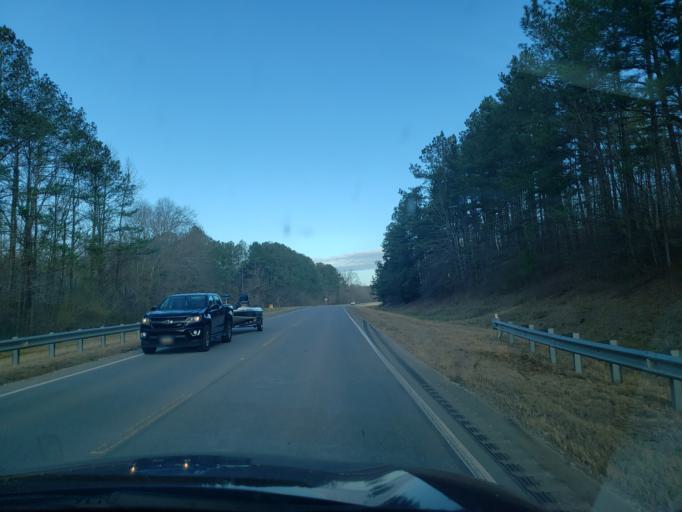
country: US
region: Alabama
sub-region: Cleburne County
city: Heflin
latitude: 33.5101
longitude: -85.6255
